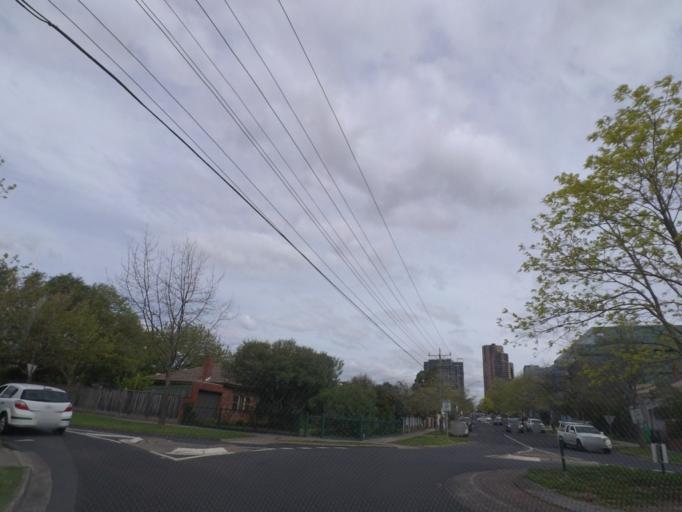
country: AU
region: Victoria
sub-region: Whitehorse
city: Box Hill
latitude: -37.8120
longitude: 145.1204
